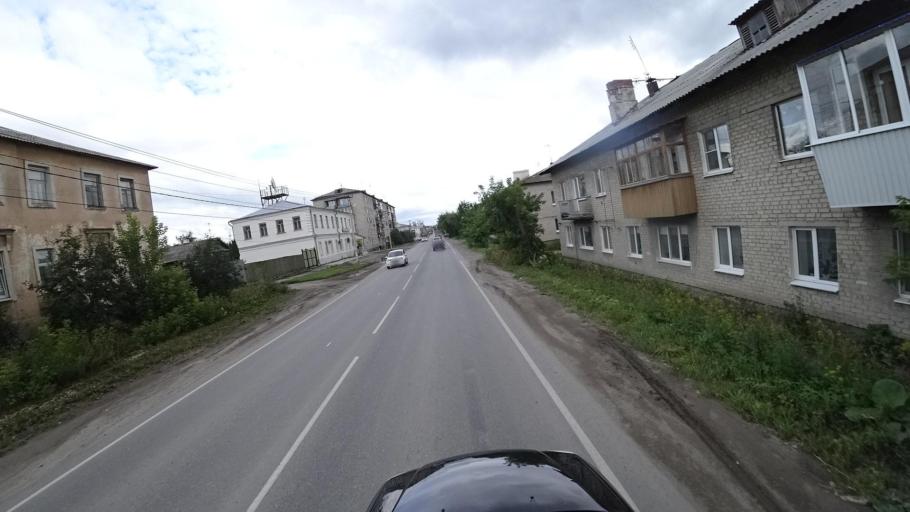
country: RU
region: Sverdlovsk
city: Kamyshlov
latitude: 56.8453
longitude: 62.6914
